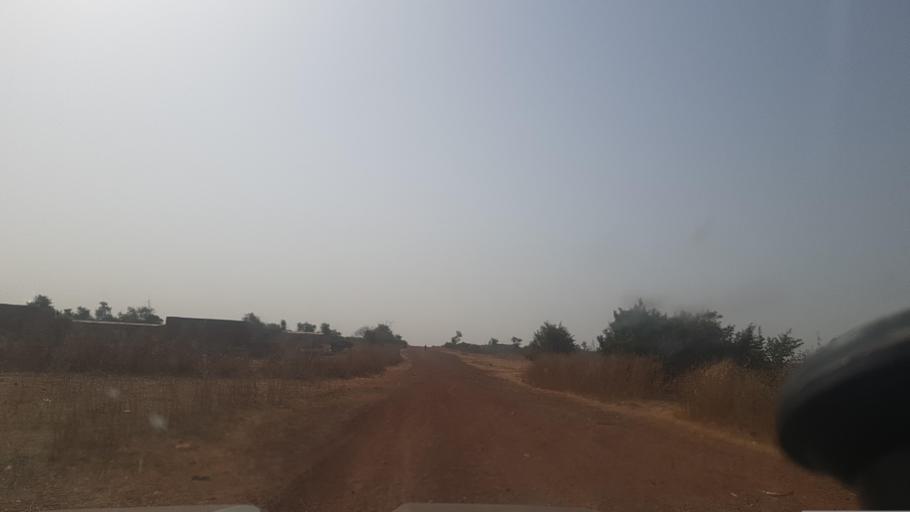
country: ML
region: Segou
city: Baroueli
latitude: 13.1621
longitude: -6.5177
